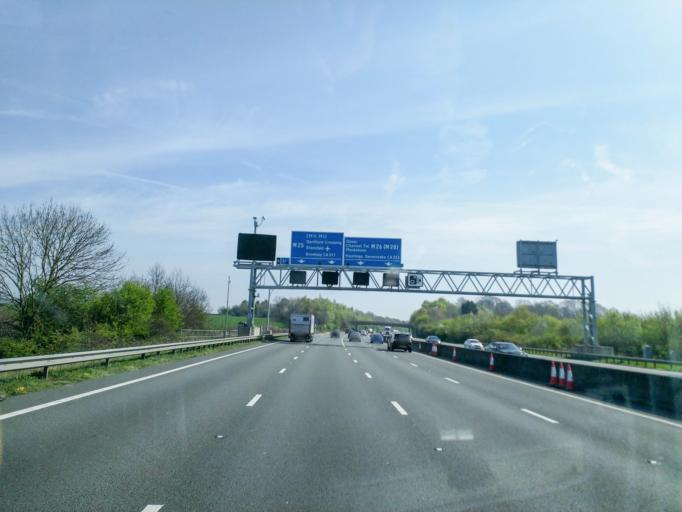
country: GB
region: England
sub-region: Kent
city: Westerham
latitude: 51.2838
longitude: 0.1063
